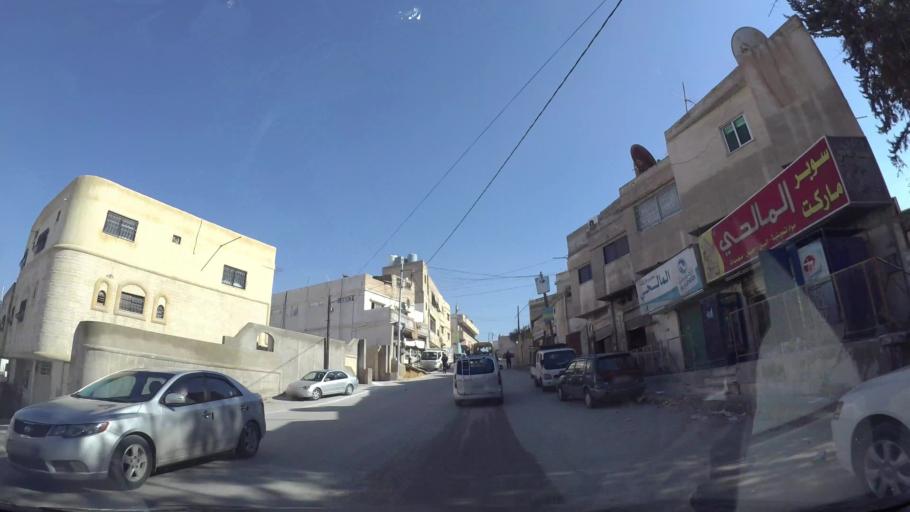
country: JO
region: Zarqa
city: Russeifa
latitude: 32.0319
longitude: 36.0395
